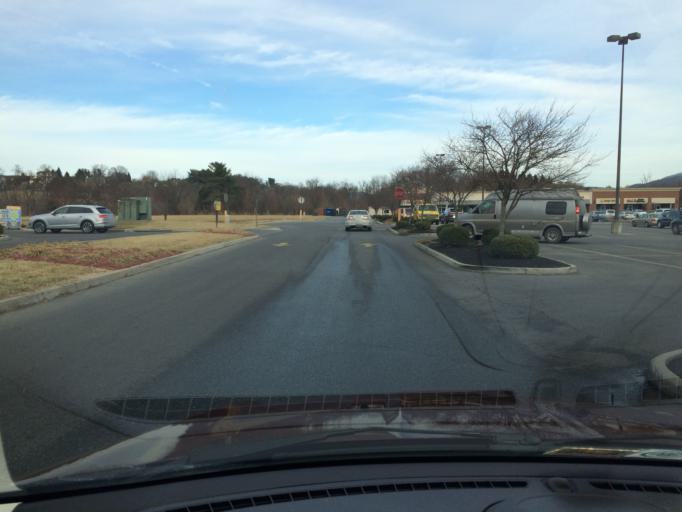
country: US
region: Virginia
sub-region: Roanoke County
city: Vinton
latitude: 37.3134
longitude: -79.8813
